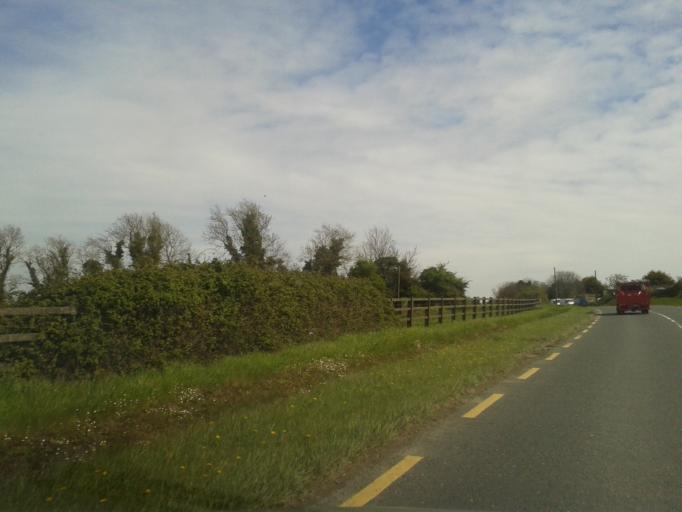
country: IE
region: Leinster
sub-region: Fingal County
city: Swords
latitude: 53.4365
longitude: -6.2369
